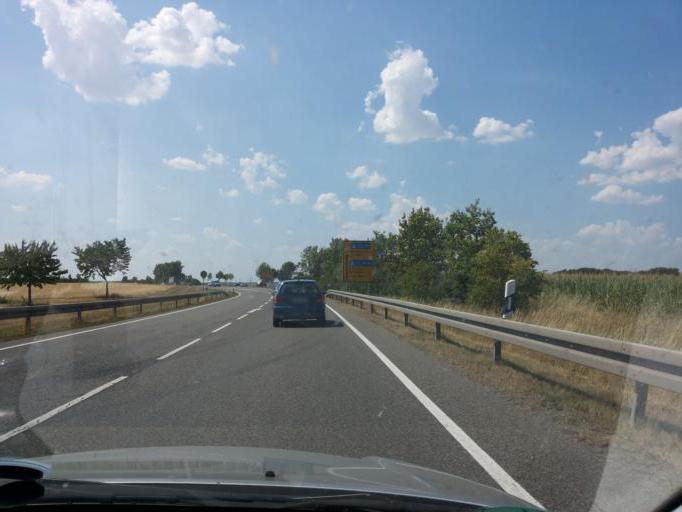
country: DE
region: Bavaria
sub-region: Regierungsbezirk Mittelfranken
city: Bad Windsheim
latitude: 49.4904
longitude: 10.3977
